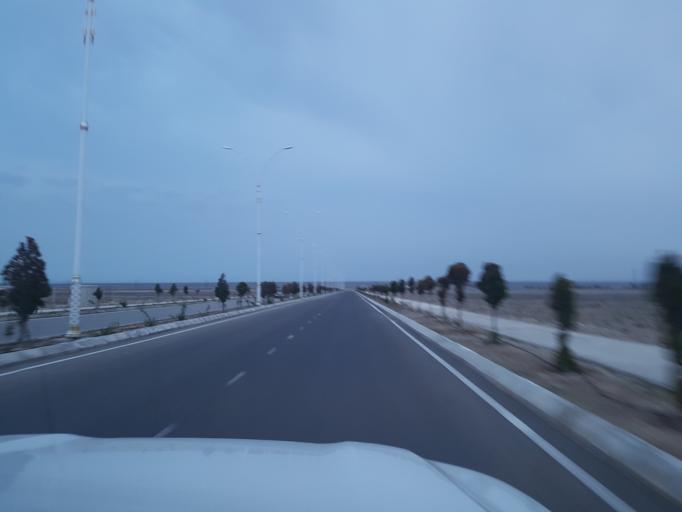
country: TM
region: Balkan
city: Balkanabat
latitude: 39.5569
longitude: 54.2960
